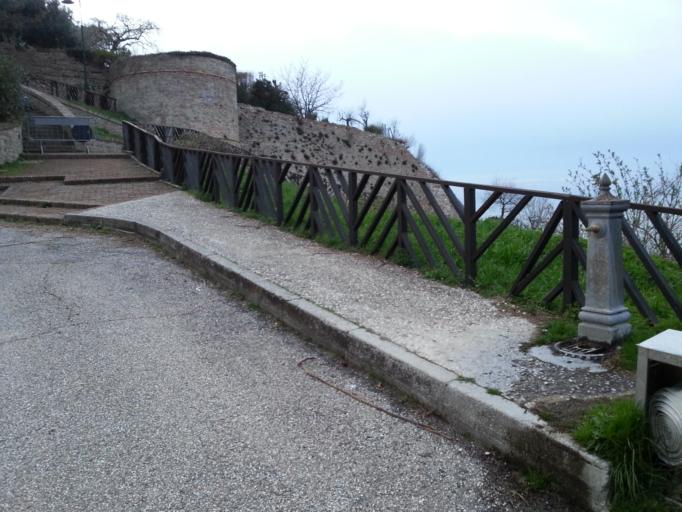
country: IT
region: The Marches
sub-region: Provincia di Pesaro e Urbino
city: Gradara
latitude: 43.9513
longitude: 12.8227
